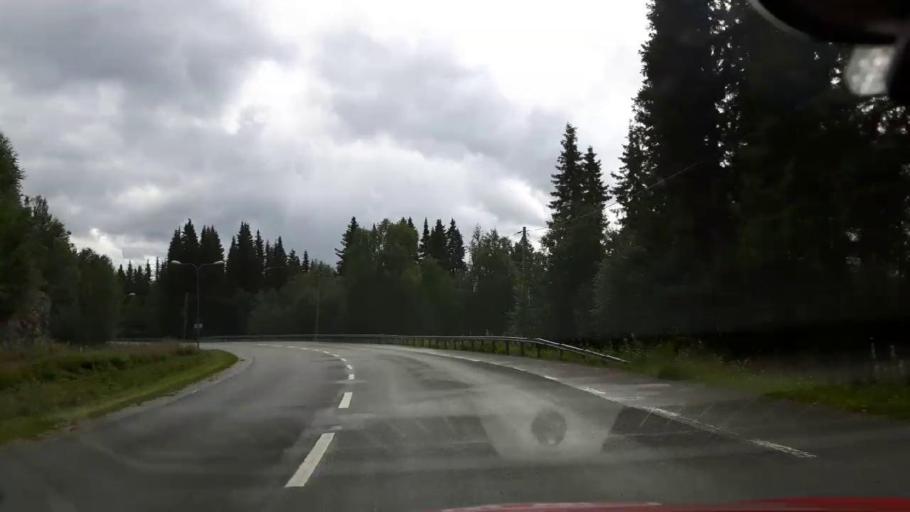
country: NO
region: Nord-Trondelag
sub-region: Lierne
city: Sandvika
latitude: 64.4940
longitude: 14.1486
